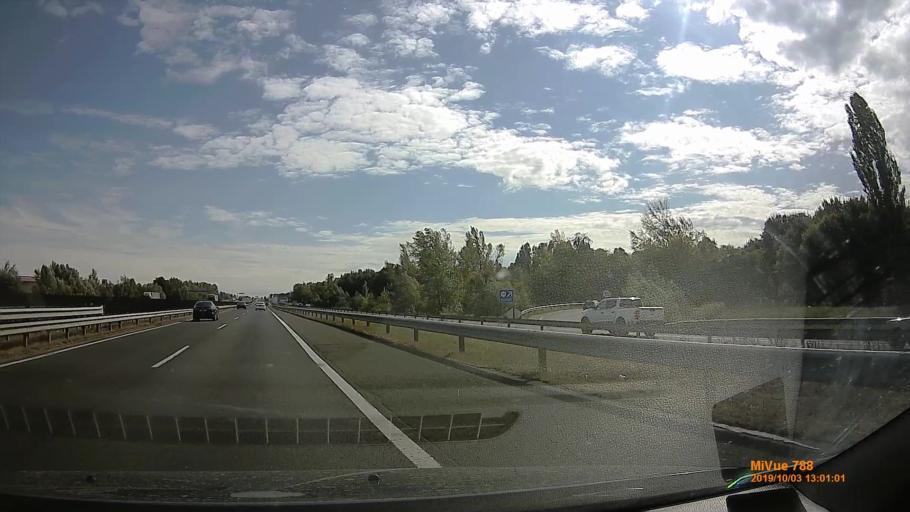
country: HU
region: Budapest
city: Budapest XV. keruelet
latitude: 47.5813
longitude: 19.1515
